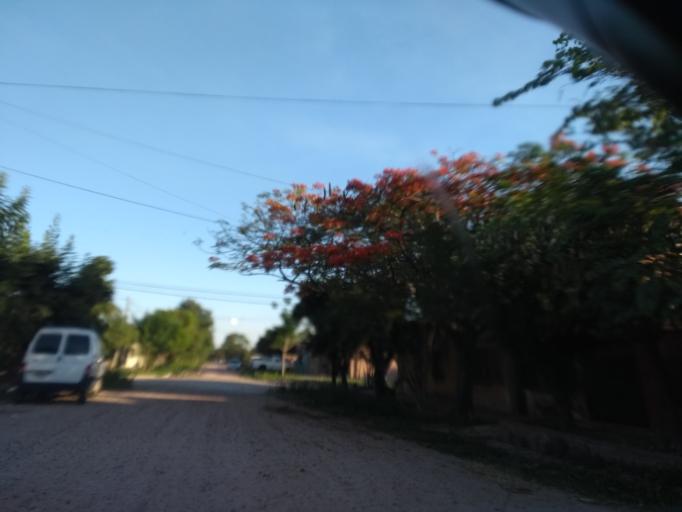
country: AR
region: Chaco
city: Barranqueras
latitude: -27.4852
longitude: -58.9429
